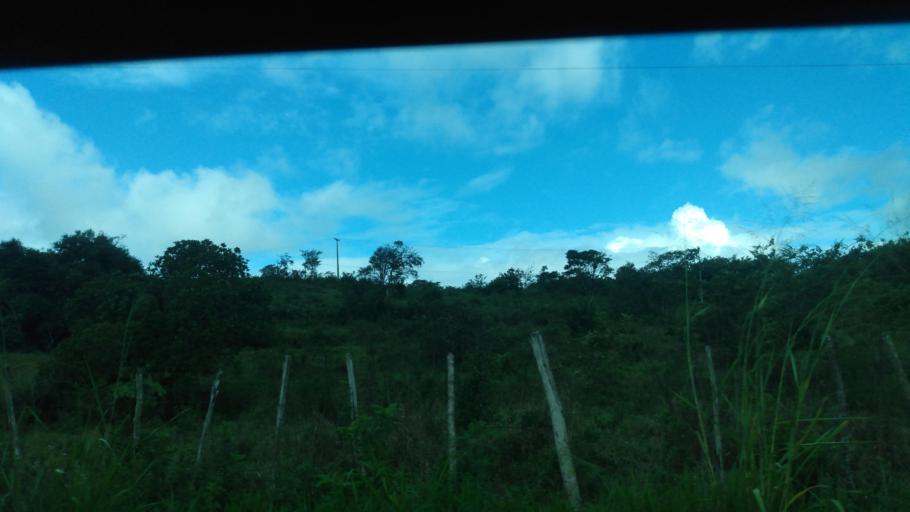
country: BR
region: Pernambuco
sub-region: Quipapa
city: Quipapa
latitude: -8.7870
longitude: -35.9617
